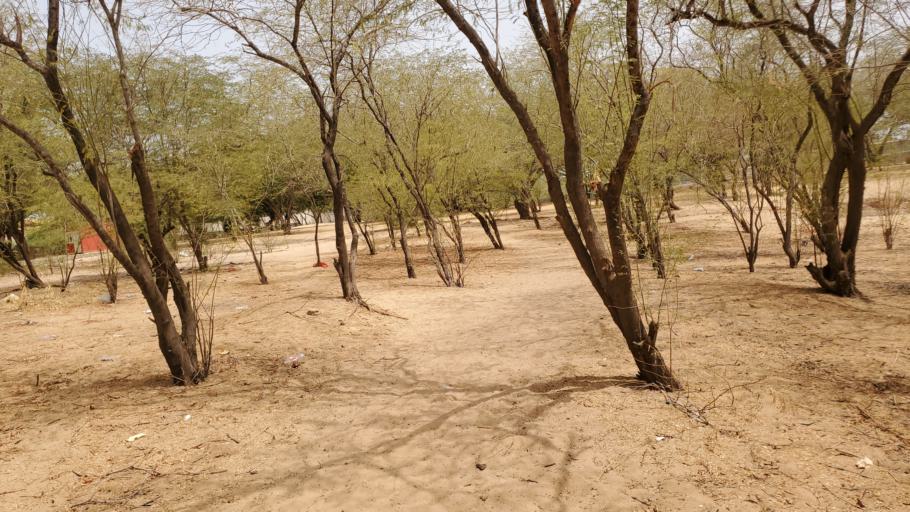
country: SN
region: Saint-Louis
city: Saint-Louis
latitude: 16.0619
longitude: -16.4197
